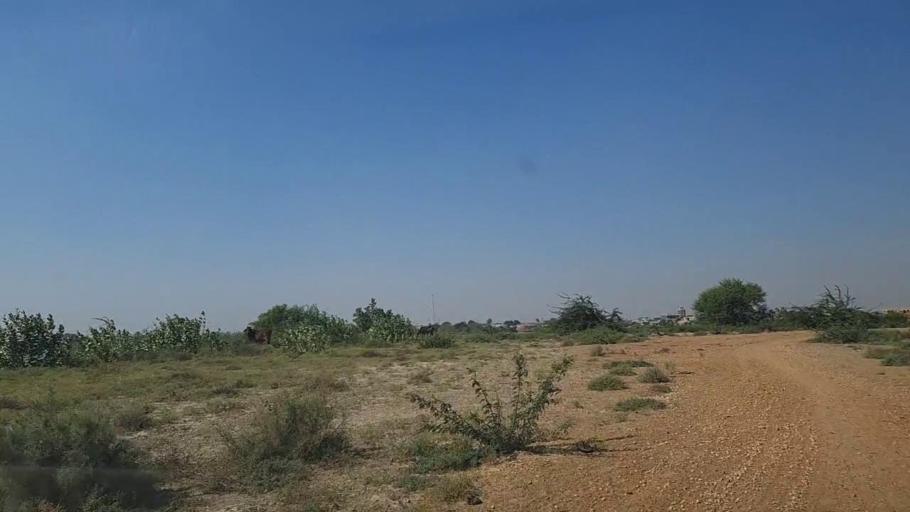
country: PK
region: Sindh
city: Thatta
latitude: 24.8103
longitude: 67.9865
